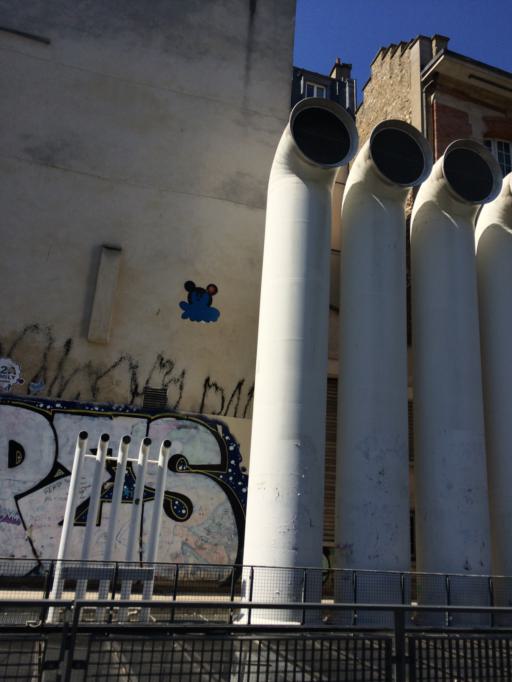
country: FR
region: Ile-de-France
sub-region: Paris
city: Paris
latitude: 48.8597
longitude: 2.3512
